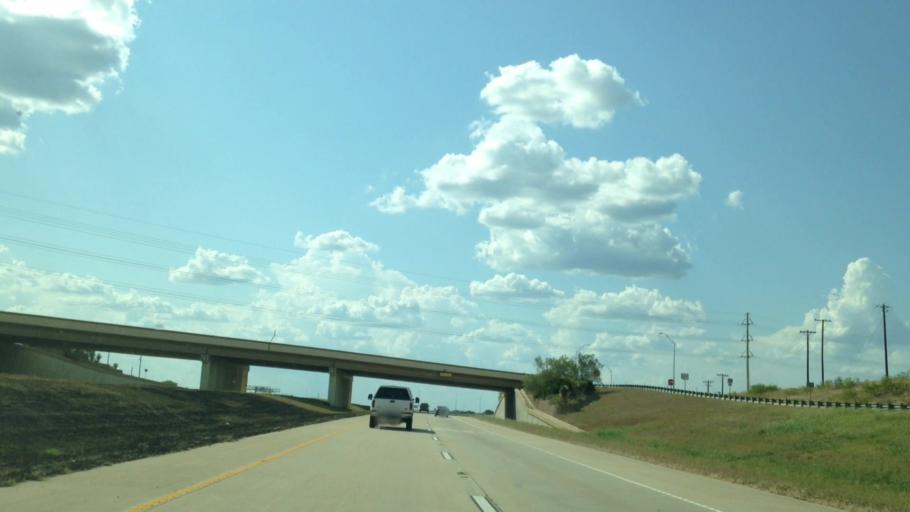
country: US
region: Texas
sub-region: Travis County
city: Onion Creek
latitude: 30.1008
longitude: -97.7783
